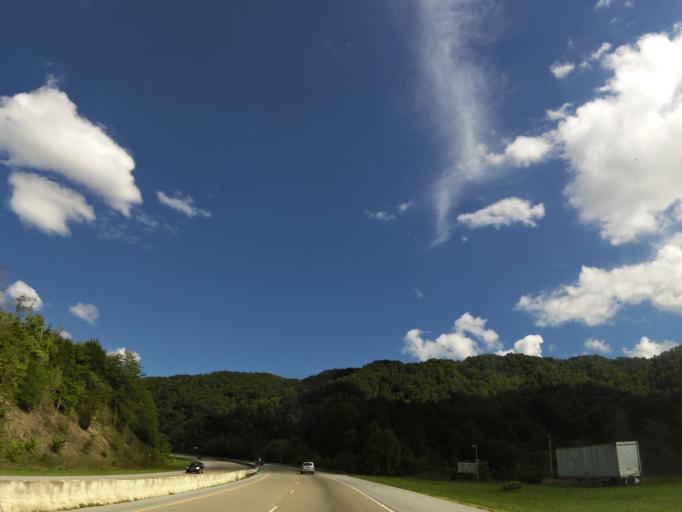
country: US
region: Tennessee
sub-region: Grainger County
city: Rutledge
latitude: 36.3479
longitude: -83.4312
